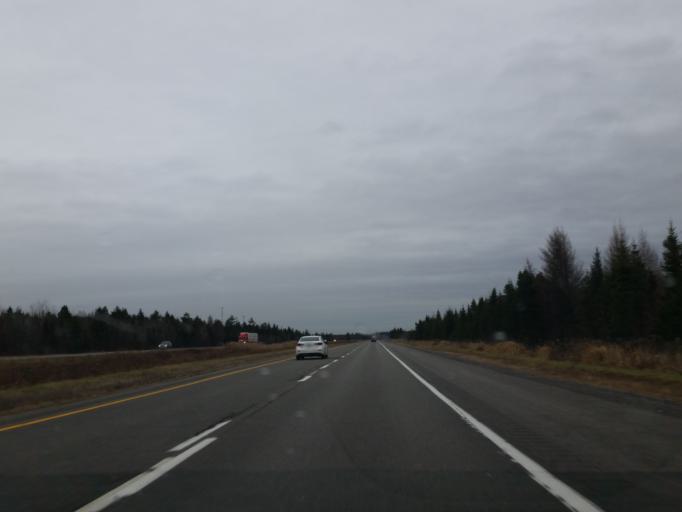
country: CA
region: Quebec
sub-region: Mauricie
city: Becancour
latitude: 46.4881
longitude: -72.3184
